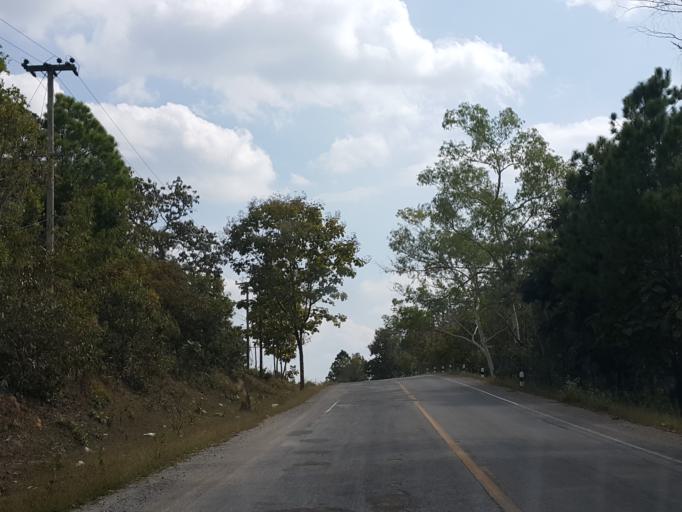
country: TH
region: Chiang Mai
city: Om Koi
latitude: 17.8452
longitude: 98.3721
